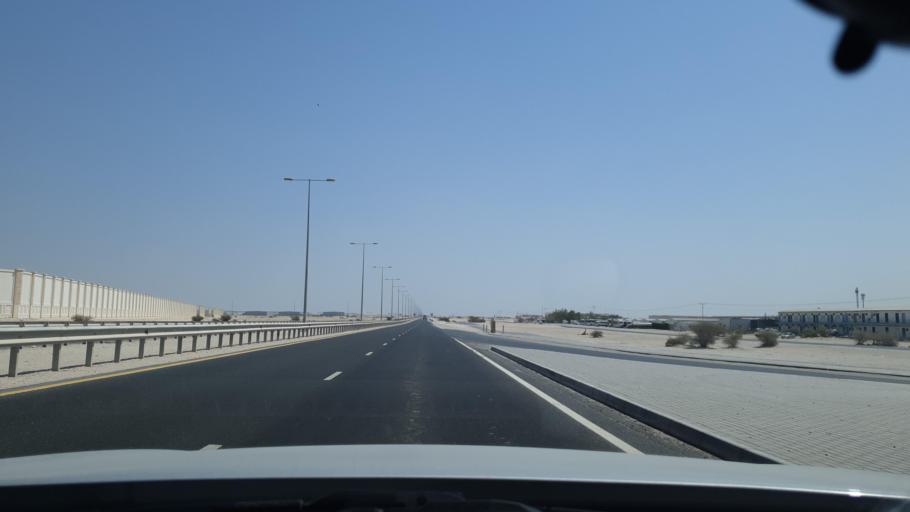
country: QA
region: Baladiyat Umm Salal
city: Umm Salal Muhammad
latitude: 25.3893
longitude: 51.3344
